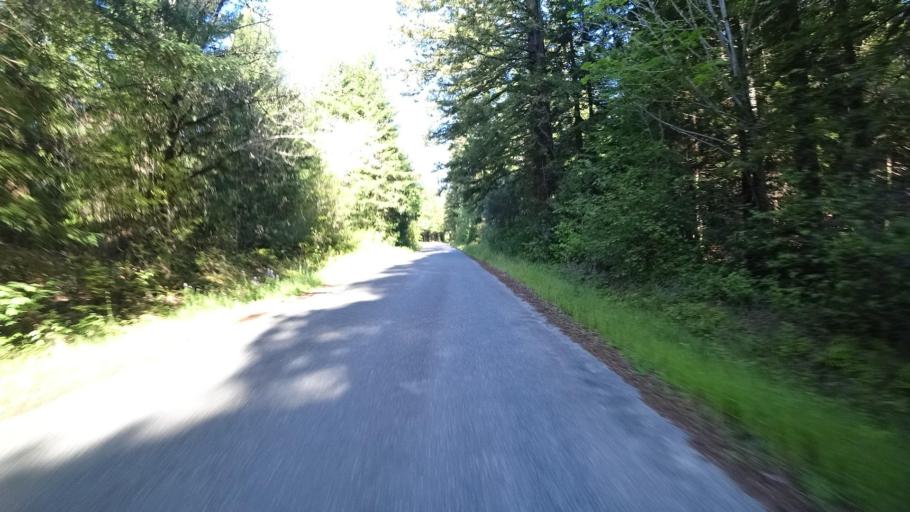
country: US
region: California
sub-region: Humboldt County
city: Rio Dell
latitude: 40.4370
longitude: -123.9657
